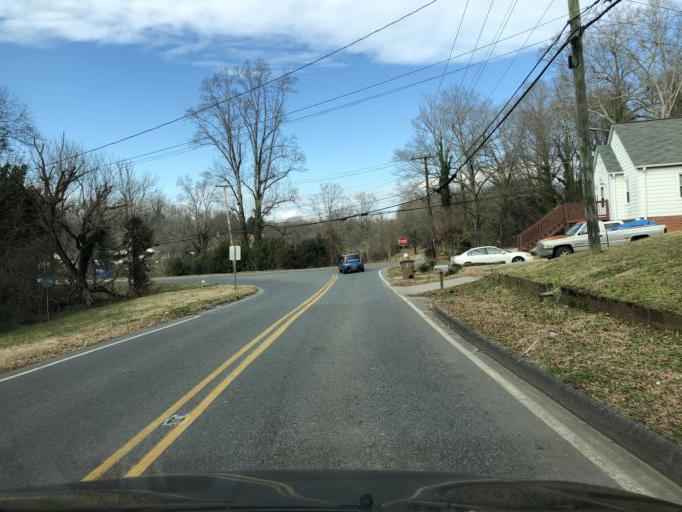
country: US
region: North Carolina
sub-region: Cleveland County
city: Shelby
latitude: 35.2886
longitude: -81.5313
